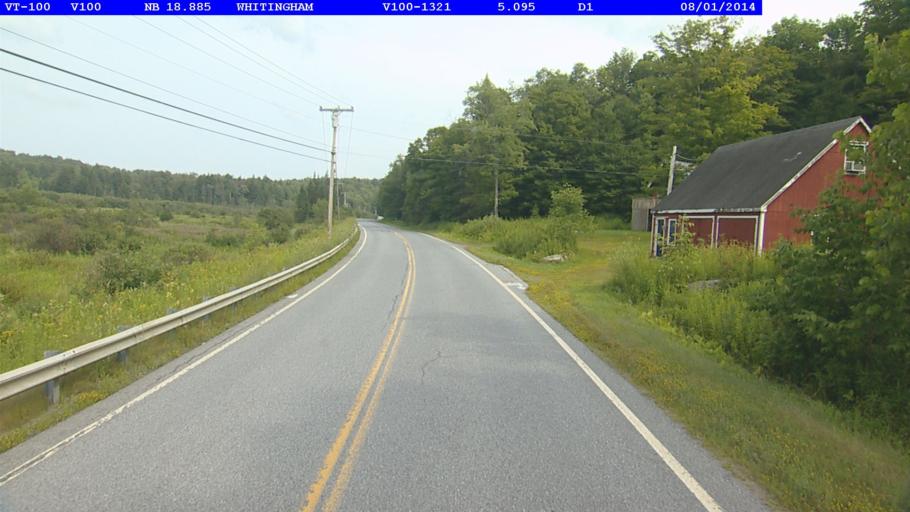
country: US
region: Massachusetts
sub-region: Franklin County
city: Charlemont
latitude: 42.7888
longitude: -72.8654
